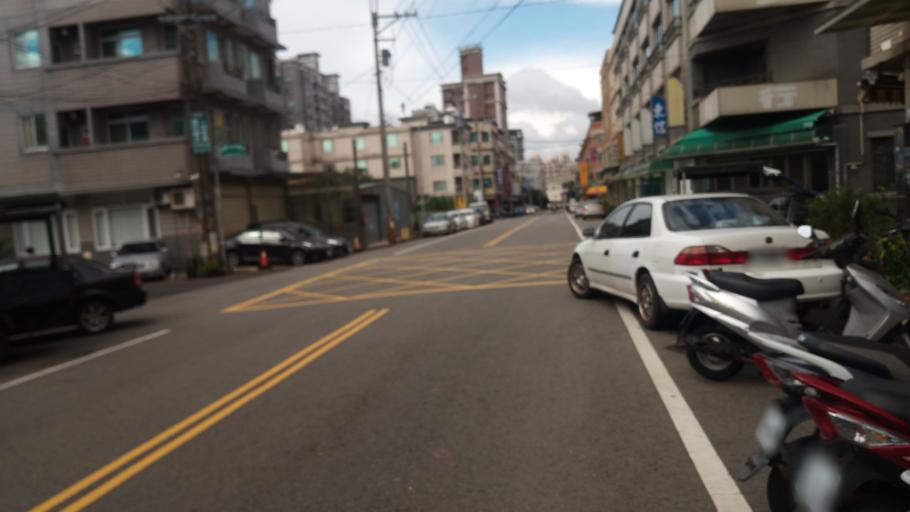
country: TW
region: Taiwan
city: Daxi
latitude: 24.9349
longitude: 121.2467
